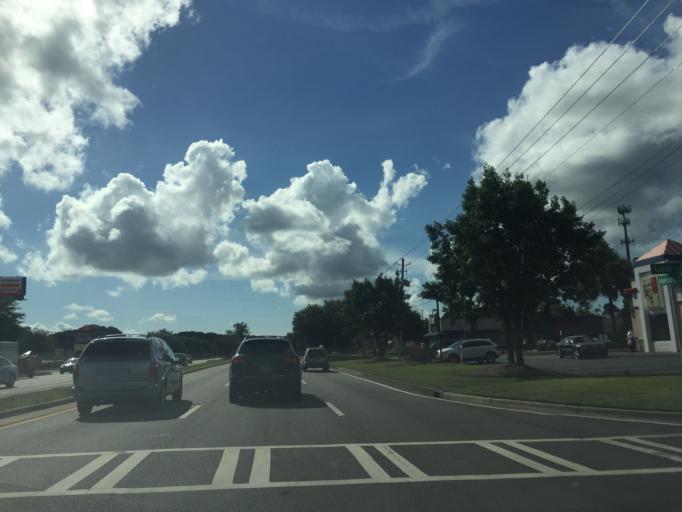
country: US
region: Georgia
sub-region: Chatham County
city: Montgomery
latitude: 31.9816
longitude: -81.1485
